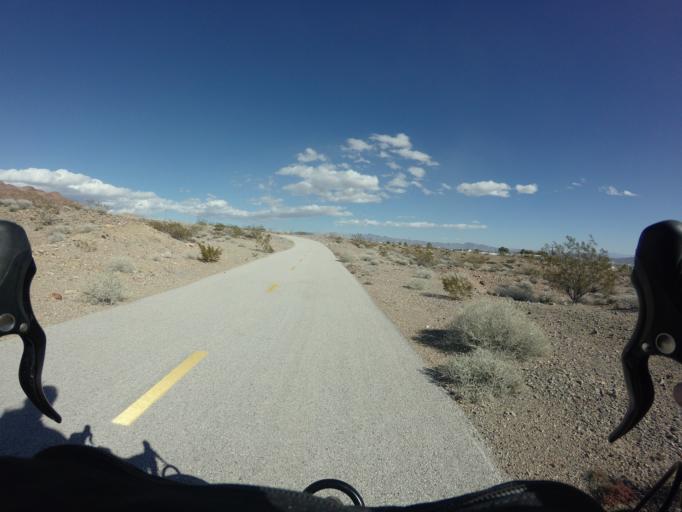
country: US
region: Nevada
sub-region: Clark County
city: Boulder City
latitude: 35.9719
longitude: -114.8731
